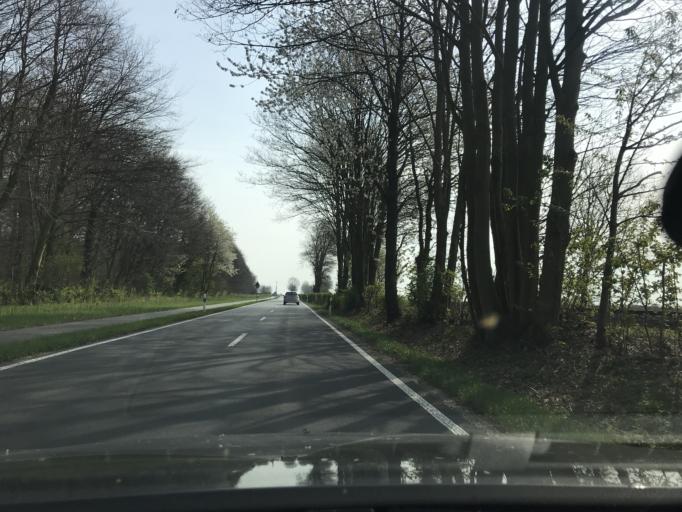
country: DE
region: North Rhine-Westphalia
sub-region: Regierungsbezirk Dusseldorf
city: Goch
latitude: 51.7323
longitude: 6.1669
